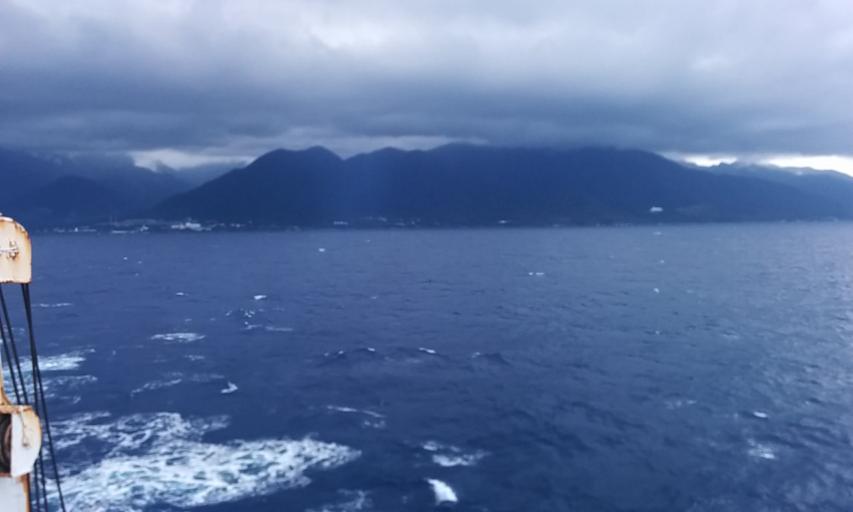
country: JP
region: Kagoshima
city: Nishinoomote
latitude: 30.4572
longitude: 130.5848
